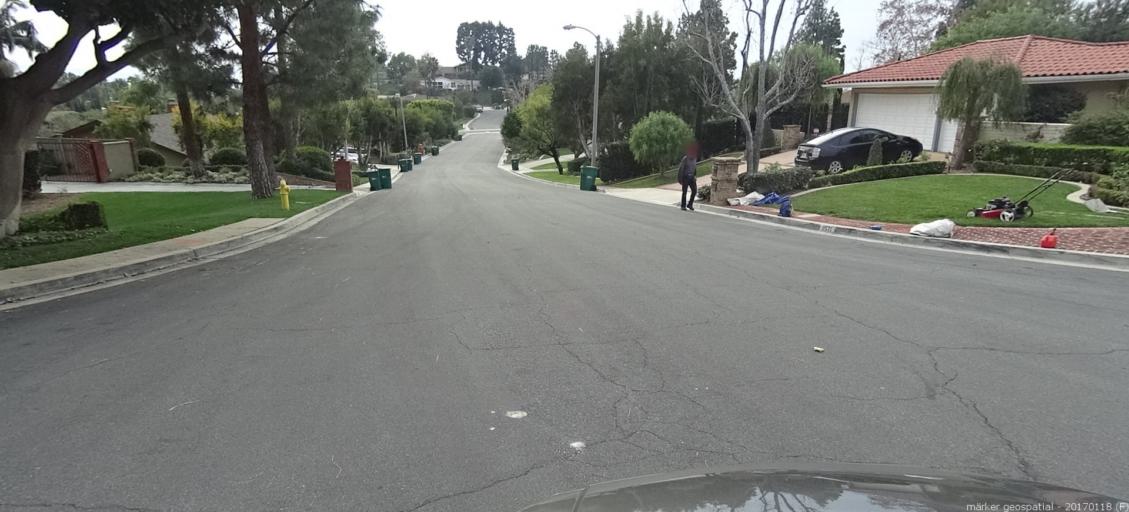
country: US
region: California
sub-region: Orange County
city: North Tustin
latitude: 33.7557
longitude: -117.7807
